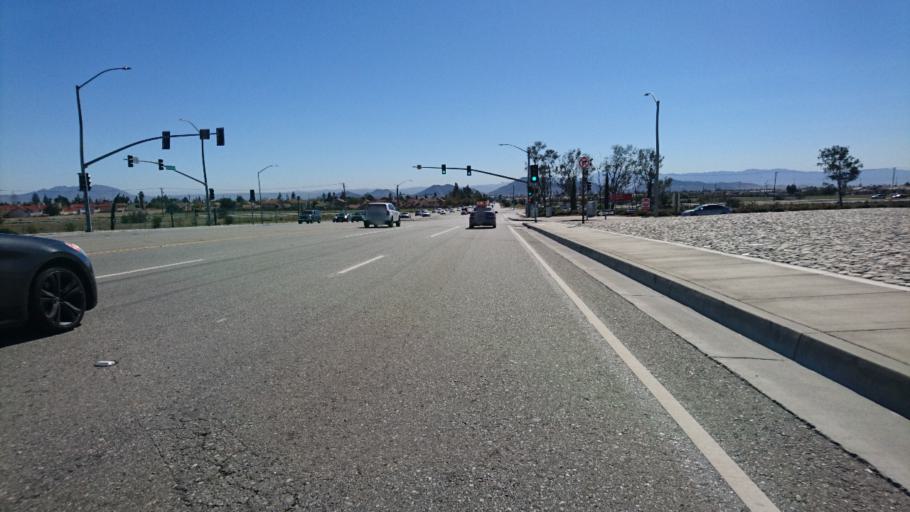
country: US
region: California
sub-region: San Bernardino County
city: Fontana
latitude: 34.1356
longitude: -117.4362
